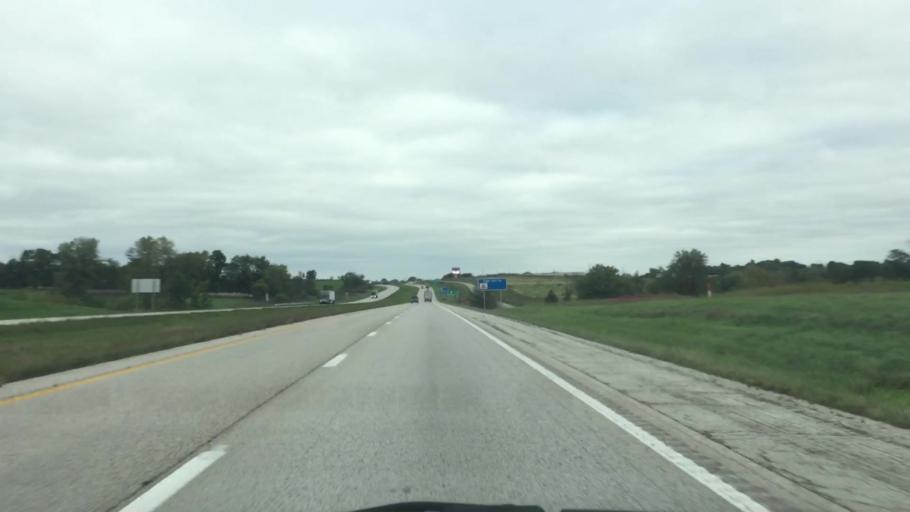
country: US
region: Missouri
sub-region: Clinton County
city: Cameron
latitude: 39.7198
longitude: -94.2225
